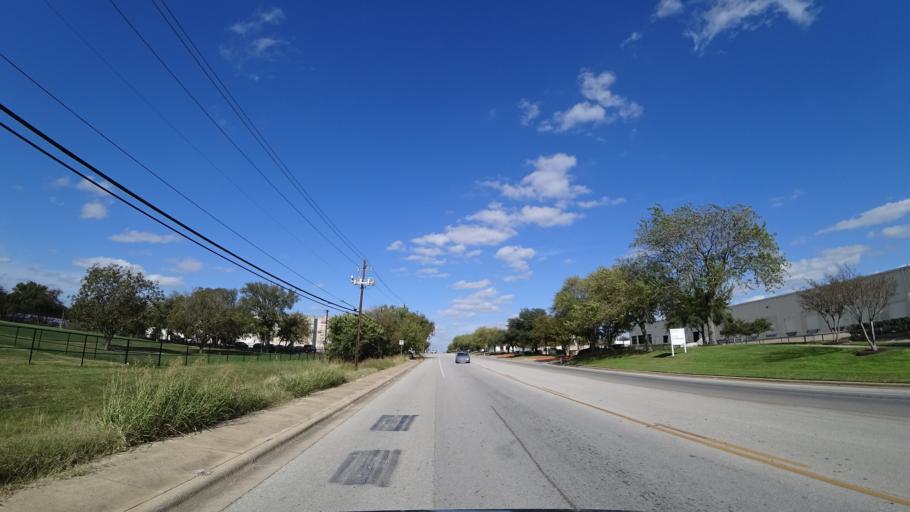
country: US
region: Texas
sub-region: Travis County
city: Wells Branch
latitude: 30.4555
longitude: -97.6791
